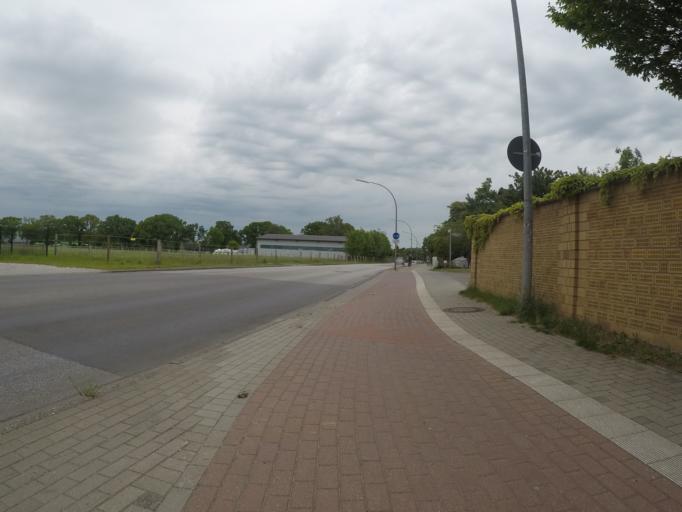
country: DE
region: Schleswig-Holstein
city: Norderstedt
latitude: 53.6813
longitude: 9.9703
